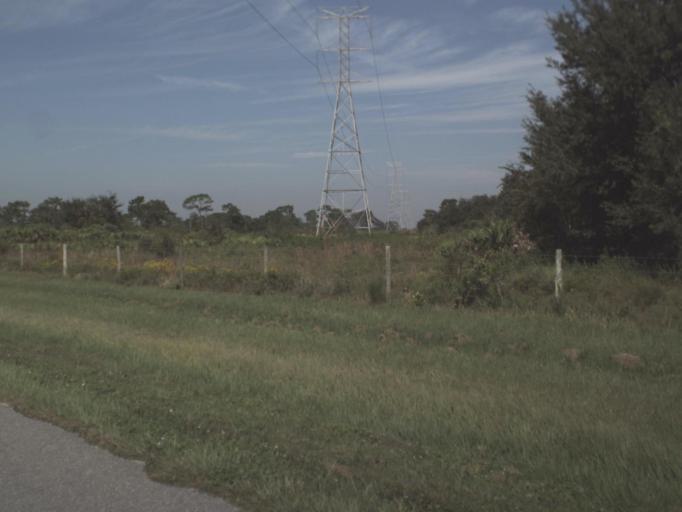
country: US
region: Florida
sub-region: Highlands County
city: Avon Park
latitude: 27.5919
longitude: -81.5690
